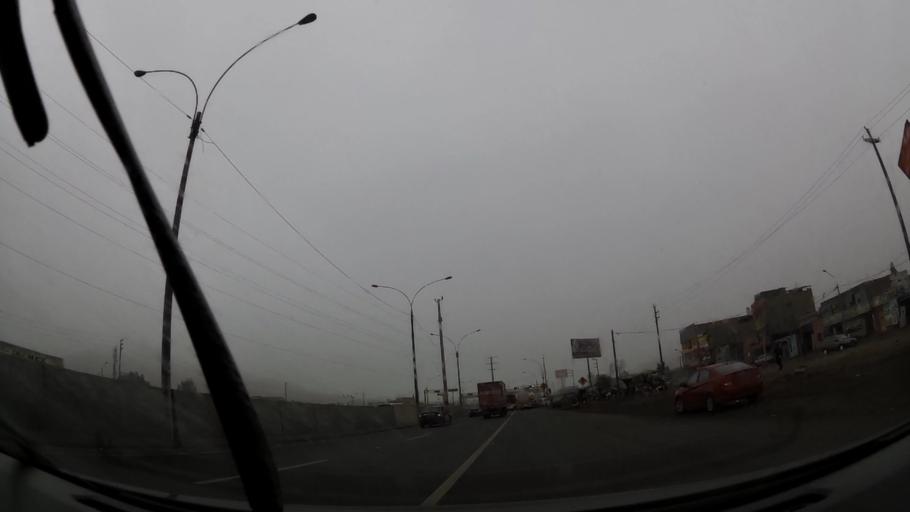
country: PE
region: Lima
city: Ventanilla
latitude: -11.8344
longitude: -77.1128
